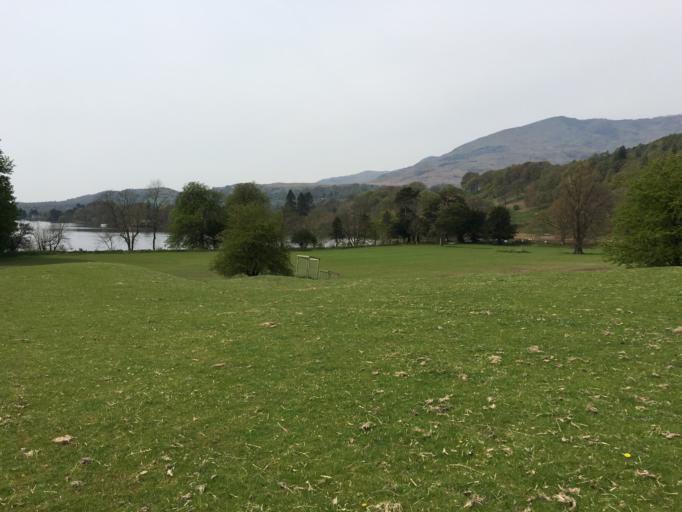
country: GB
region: England
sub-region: Cumbria
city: Ambleside
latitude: 54.3731
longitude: -3.0529
